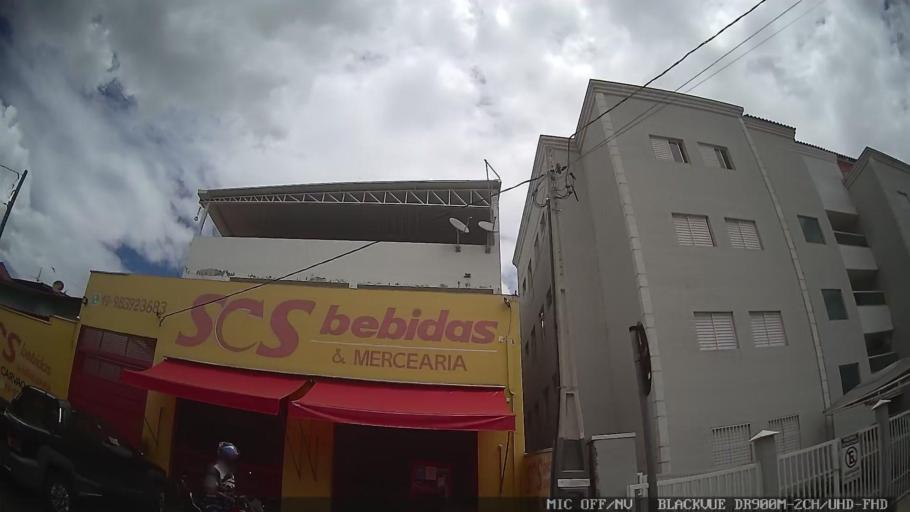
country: BR
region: Sao Paulo
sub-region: Jaguariuna
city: Jaguariuna
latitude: -22.7065
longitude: -46.9638
